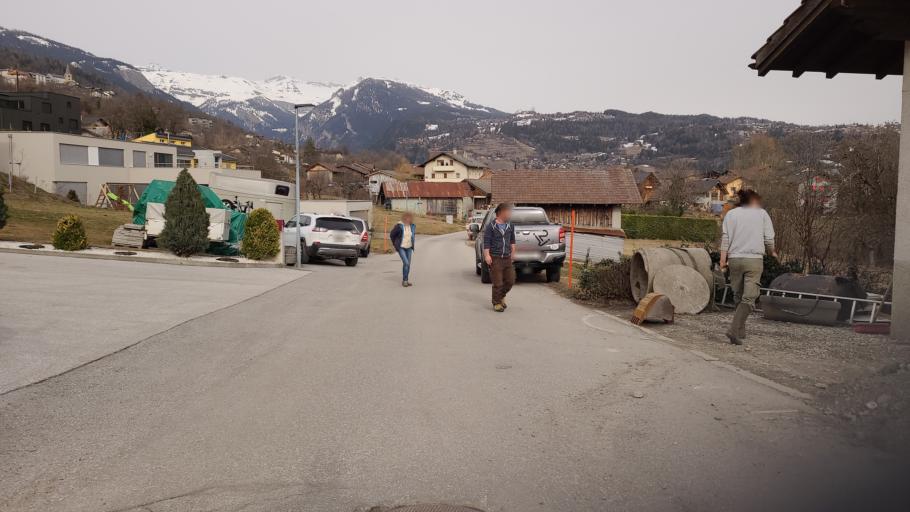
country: CH
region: Valais
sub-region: Herens District
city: Ayent
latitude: 46.2733
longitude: 7.4094
